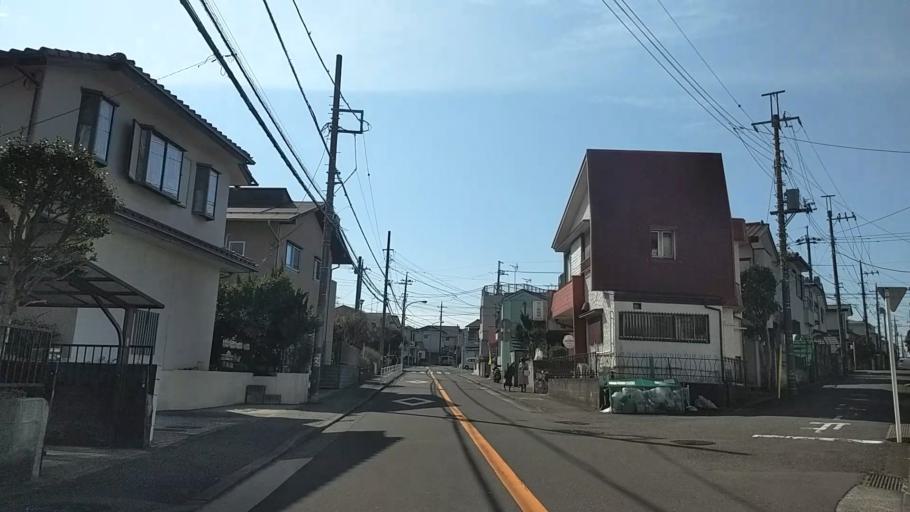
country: JP
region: Kanagawa
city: Kamakura
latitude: 35.3953
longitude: 139.5566
